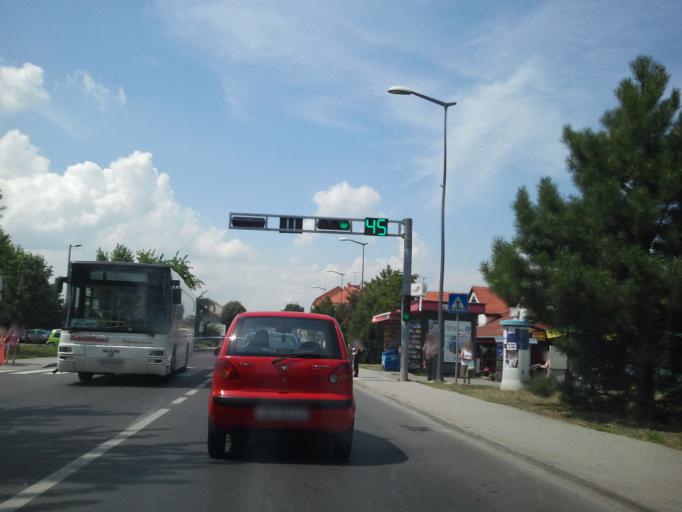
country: HR
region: Vukovarsko-Srijemska
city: Vukovar
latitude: 45.3519
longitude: 19.0007
